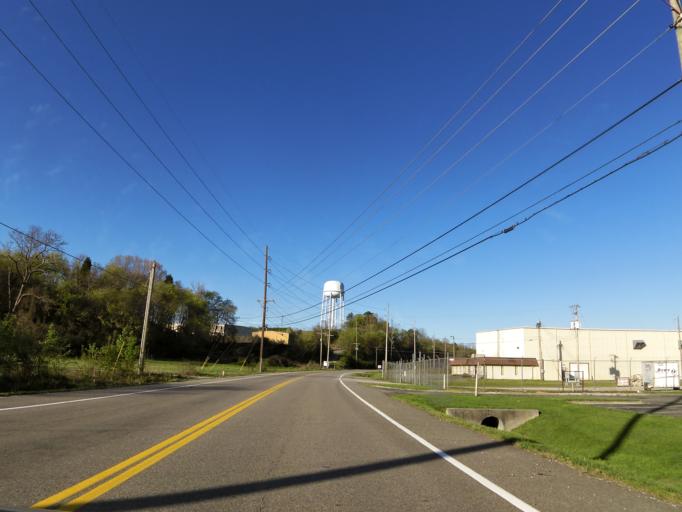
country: US
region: Tennessee
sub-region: Knox County
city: Knoxville
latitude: 35.9456
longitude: -83.8281
